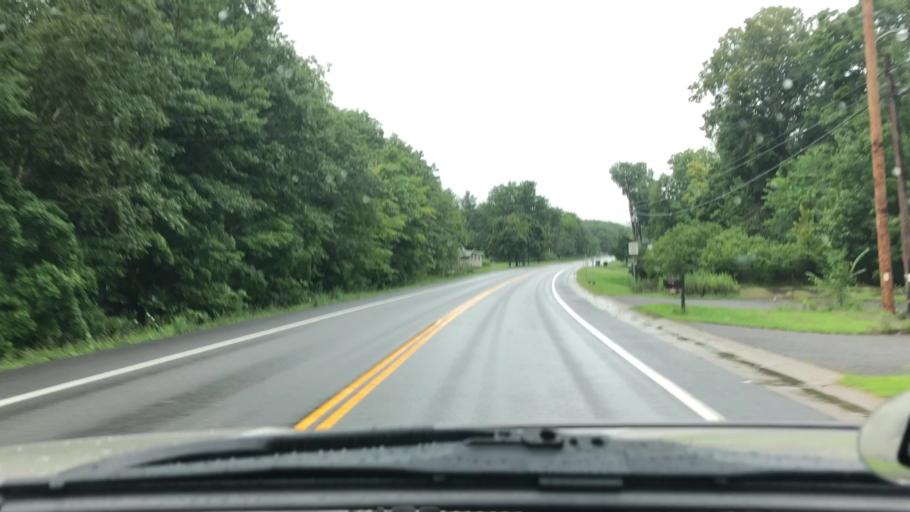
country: US
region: New York
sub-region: Greene County
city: Cairo
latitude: 42.3212
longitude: -74.0881
